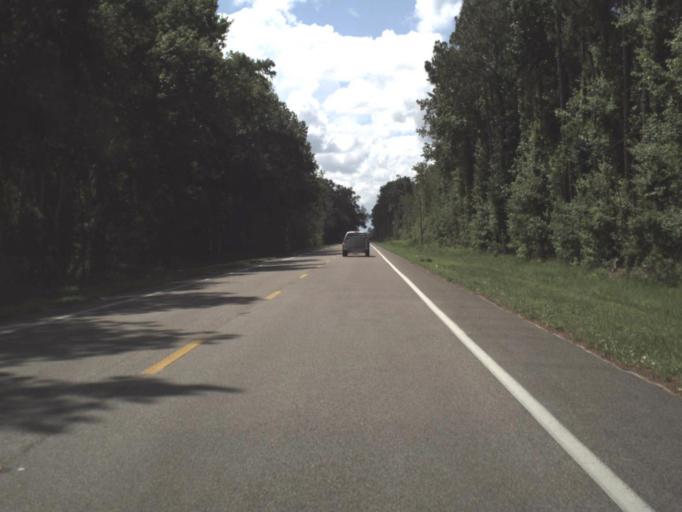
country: US
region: Florida
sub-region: Putnam County
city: Crescent City
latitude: 29.5469
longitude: -81.5290
